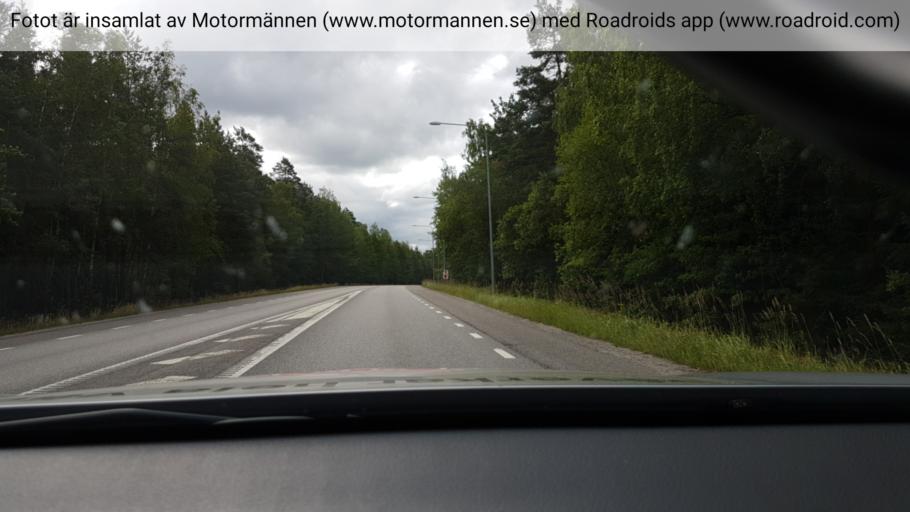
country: SE
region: Stockholm
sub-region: Nacka Kommun
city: Alta
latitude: 59.2388
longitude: 18.1873
